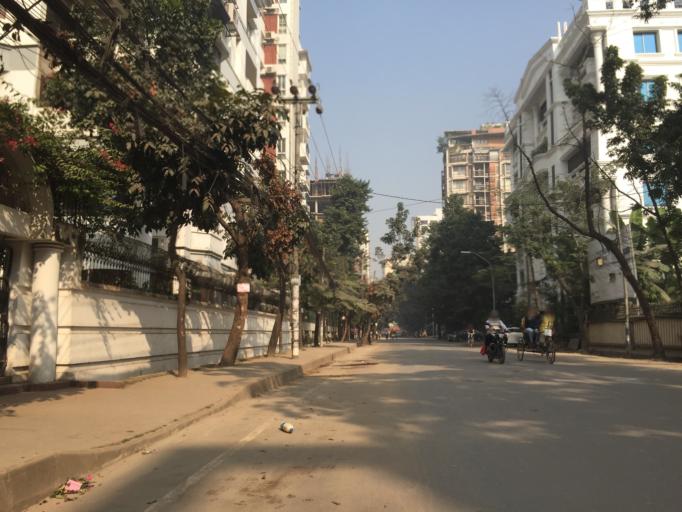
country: BD
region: Dhaka
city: Paltan
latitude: 23.7909
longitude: 90.4133
